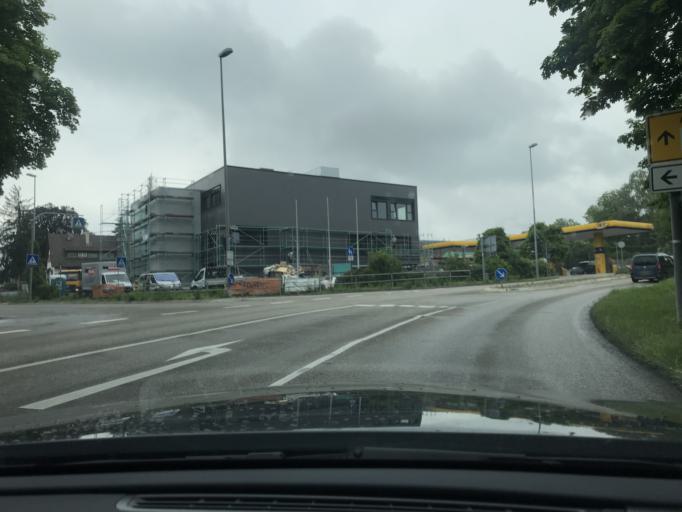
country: DE
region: Baden-Wuerttemberg
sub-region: Regierungsbezirk Stuttgart
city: Waiblingen
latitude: 48.8297
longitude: 9.3022
